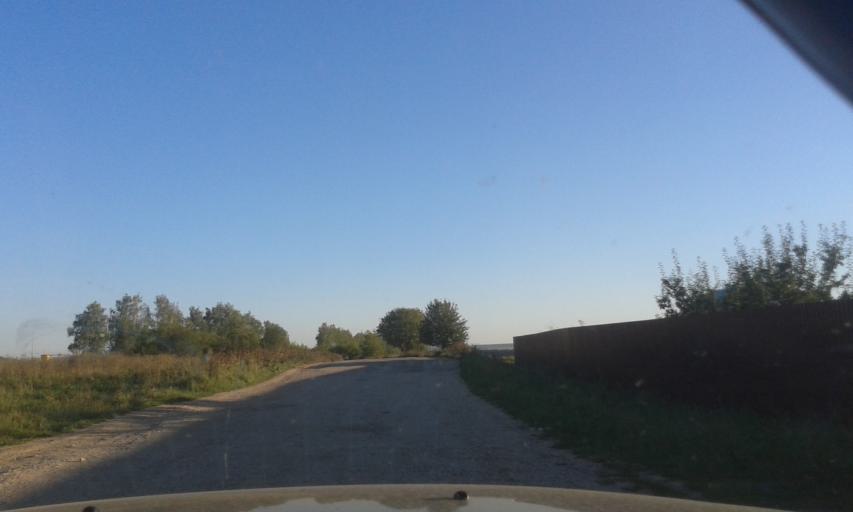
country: RU
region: Tula
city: Krapivna
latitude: 54.1349
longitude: 37.1574
